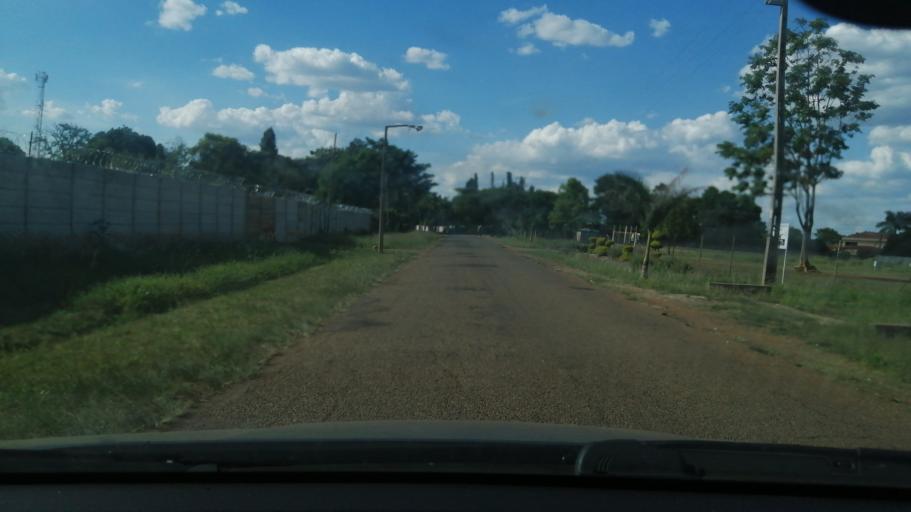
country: ZW
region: Harare
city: Harare
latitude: -17.7694
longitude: 31.0626
